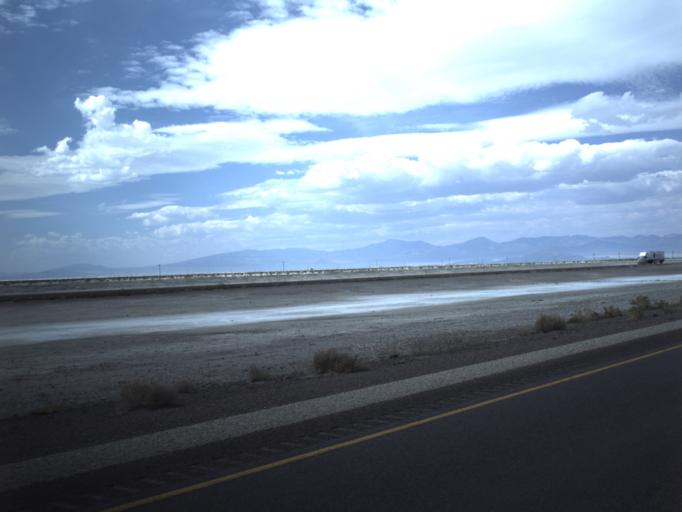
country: US
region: Utah
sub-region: Tooele County
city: Wendover
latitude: 40.7384
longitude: -113.8041
